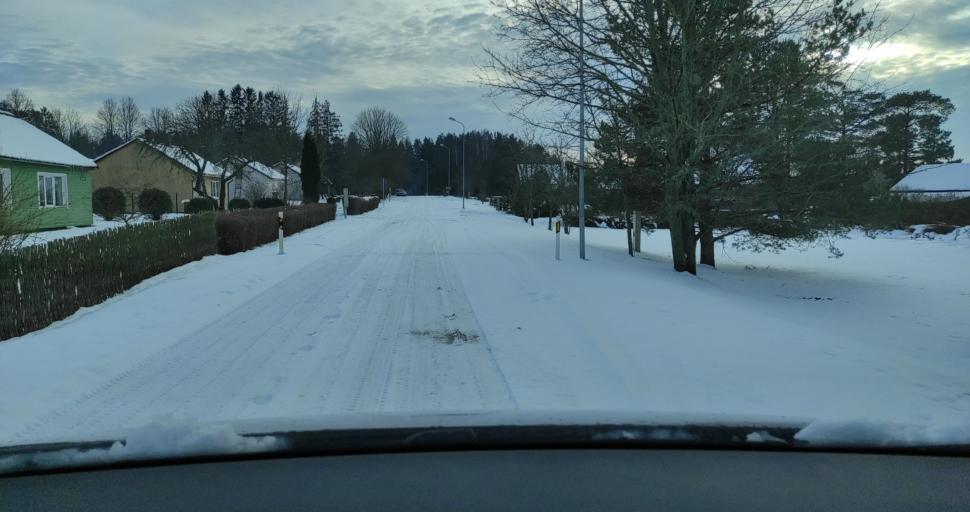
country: LV
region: Kuldigas Rajons
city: Kuldiga
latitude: 56.9004
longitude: 22.0742
